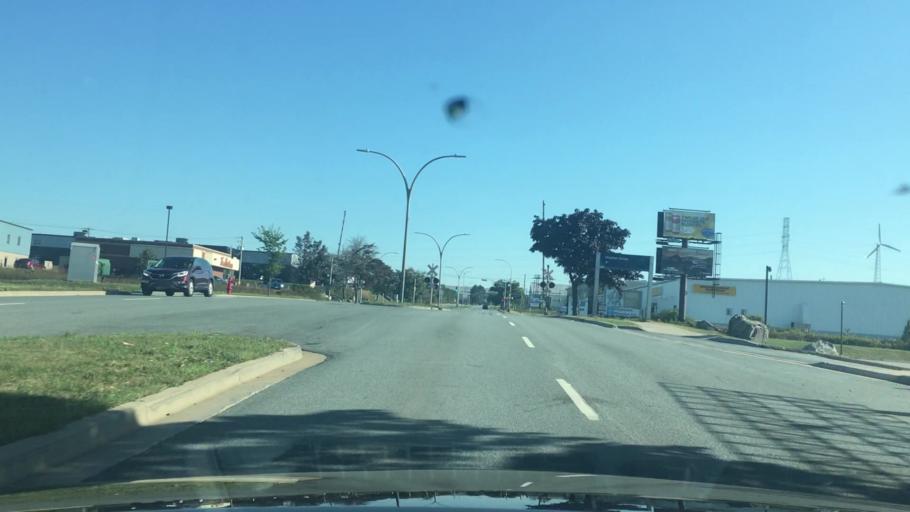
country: CA
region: Nova Scotia
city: Dartmouth
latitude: 44.7063
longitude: -63.6090
